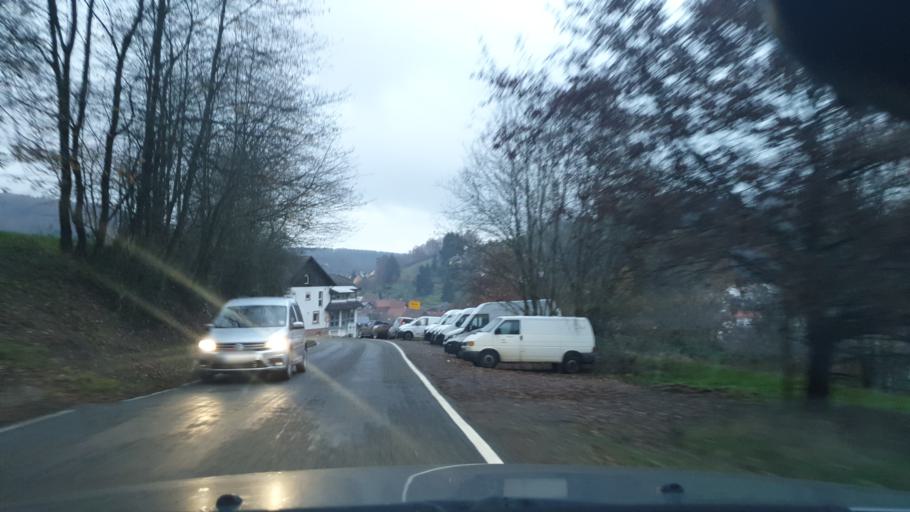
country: DE
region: Rheinland-Pfalz
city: Bann
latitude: 49.3876
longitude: 7.6108
